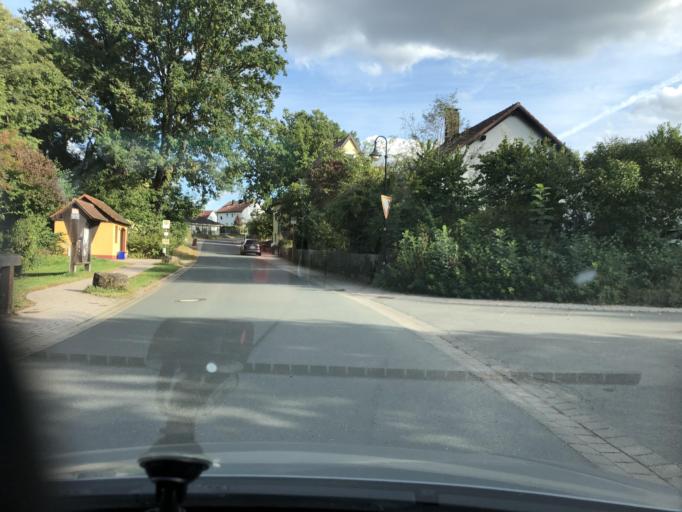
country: DE
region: Bavaria
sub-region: Regierungsbezirk Mittelfranken
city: Cadolzburg
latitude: 49.4695
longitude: 10.8456
